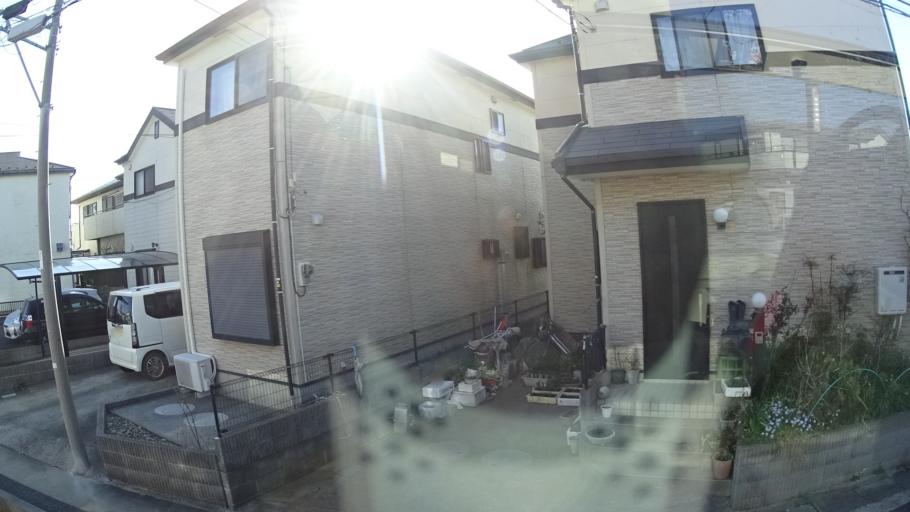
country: JP
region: Kanagawa
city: Miura
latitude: 35.1551
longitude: 139.6304
